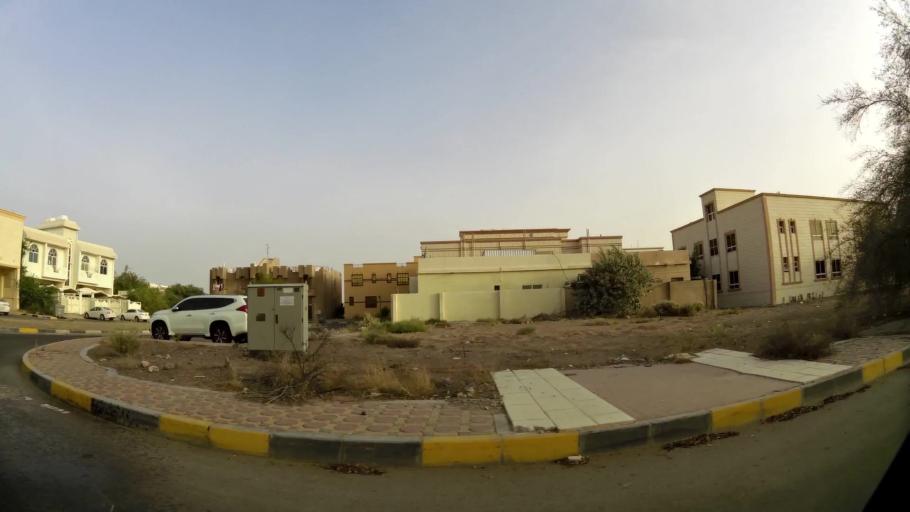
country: OM
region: Al Buraimi
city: Al Buraymi
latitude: 24.2473
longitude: 55.7301
